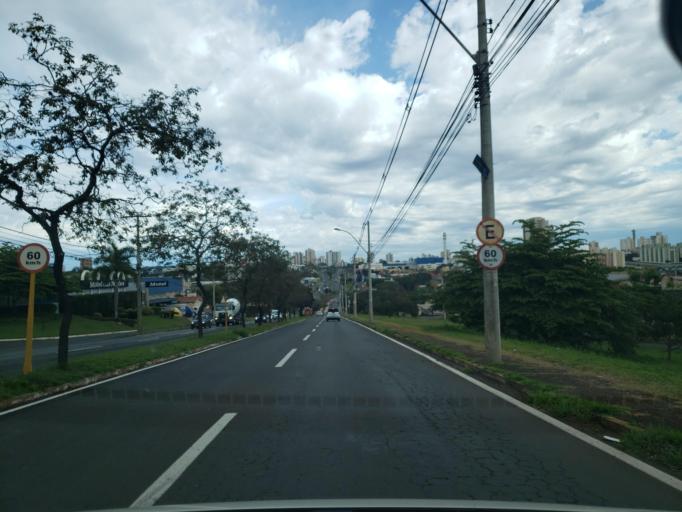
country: BR
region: Sao Paulo
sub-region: Bauru
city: Bauru
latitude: -22.3362
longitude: -49.0354
